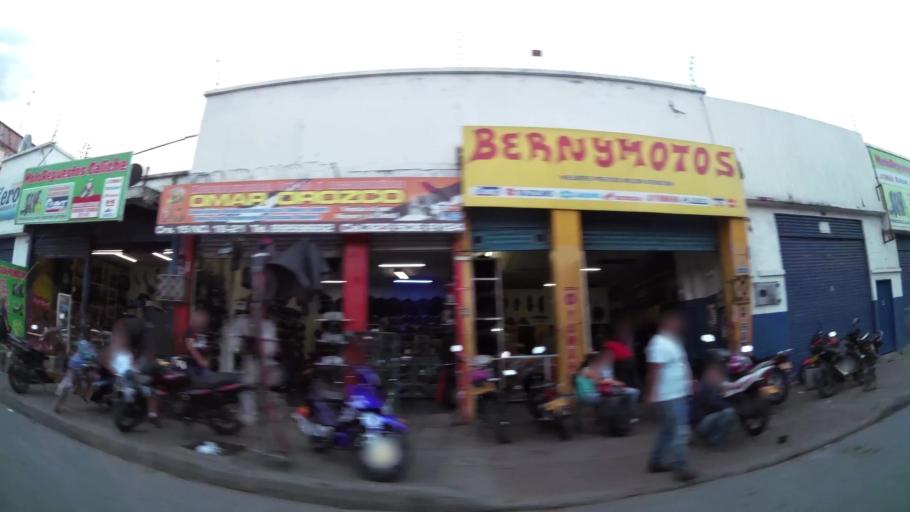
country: CO
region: Valle del Cauca
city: Cali
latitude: 3.4434
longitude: -76.5232
